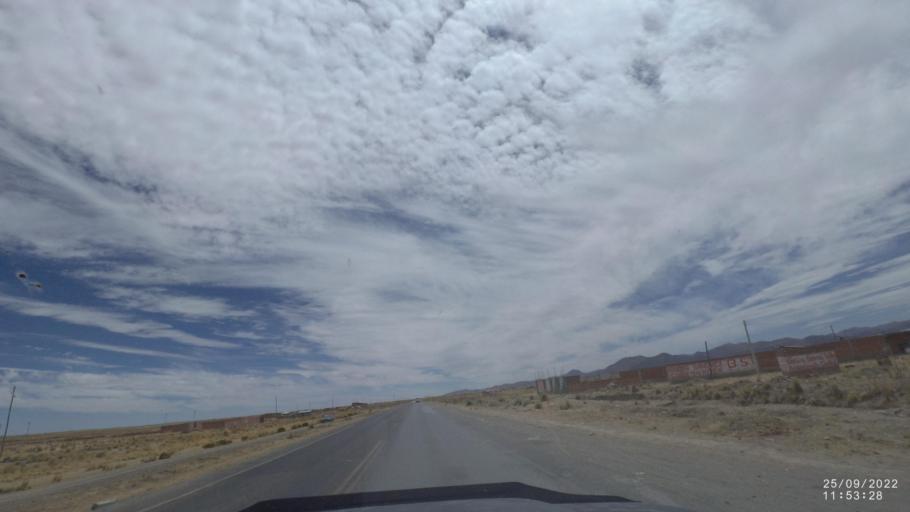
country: BO
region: Oruro
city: Challapata
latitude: -18.8892
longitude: -66.7823
